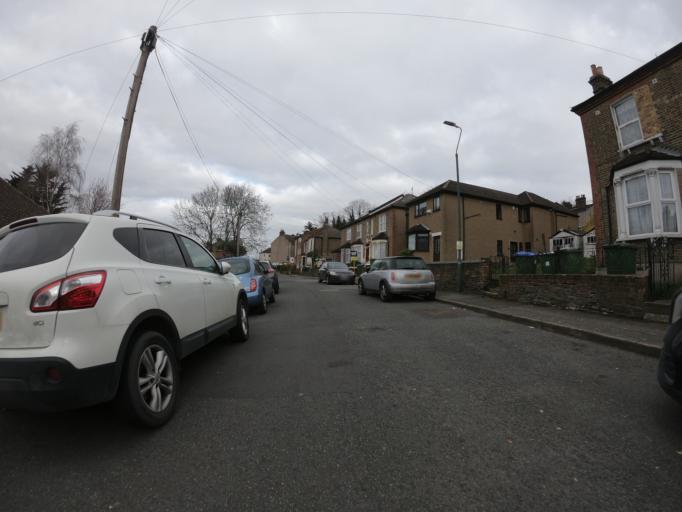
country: GB
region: England
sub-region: Greater London
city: Belvedere
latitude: 51.4881
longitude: 0.1484
